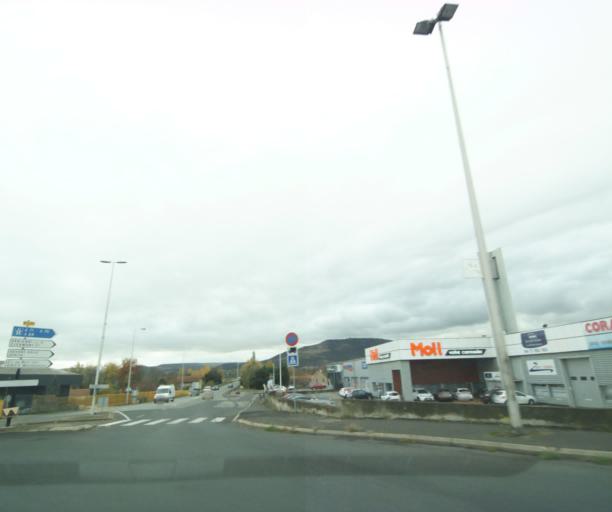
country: FR
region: Auvergne
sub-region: Departement du Puy-de-Dome
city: Cournon-d'Auvergne
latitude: 45.7398
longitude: 3.1715
